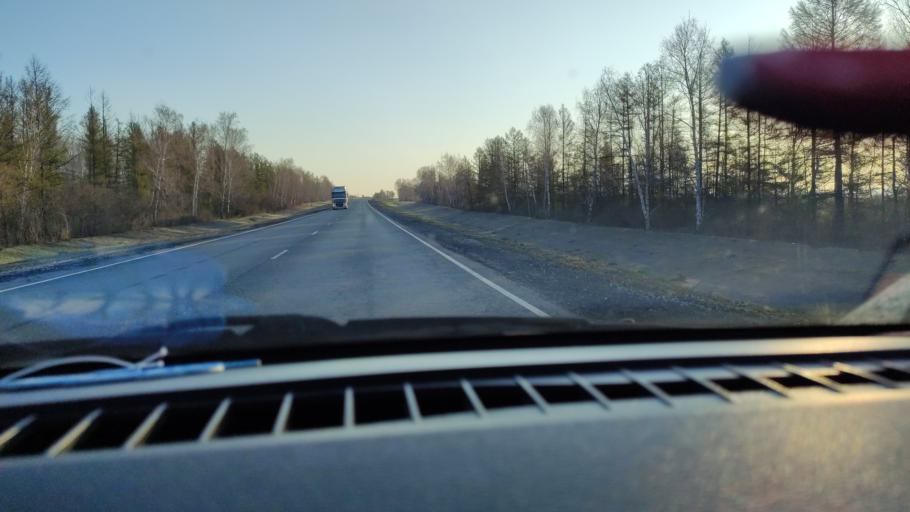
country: RU
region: Saratov
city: Sennoy
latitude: 52.1302
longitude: 46.8606
